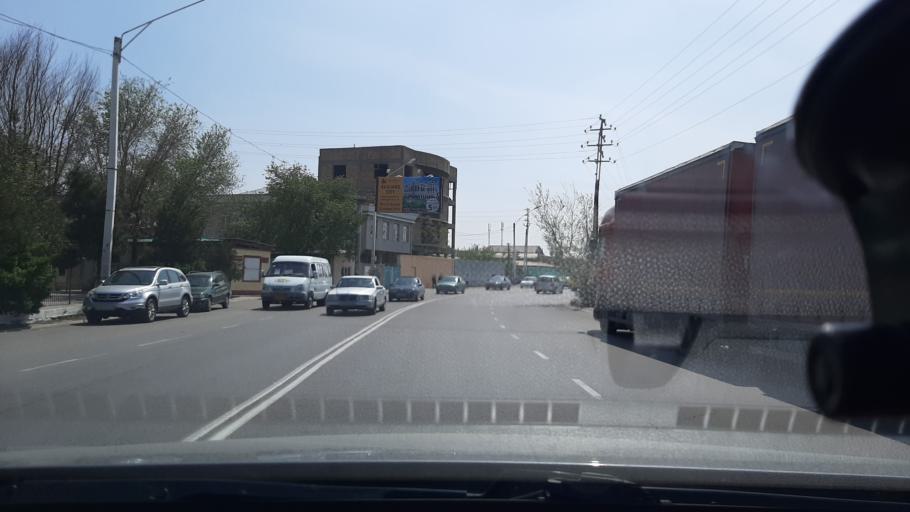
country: TJ
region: Viloyati Sughd
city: Khujand
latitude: 40.2879
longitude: 69.6423
